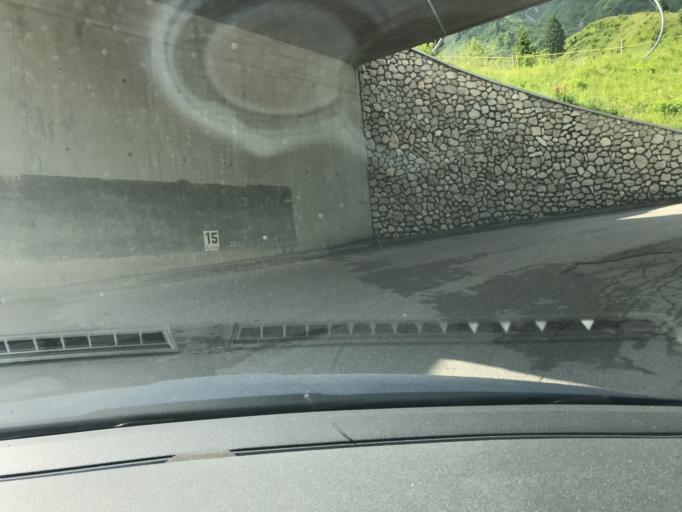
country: IT
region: Trentino-Alto Adige
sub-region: Bolzano
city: Corvara in Badia
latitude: 46.4878
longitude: 11.8456
